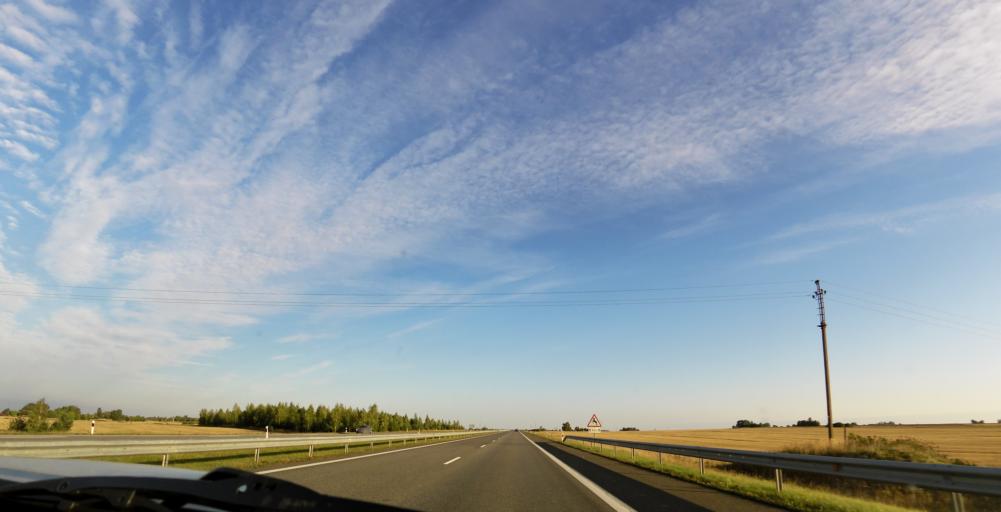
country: LT
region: Vilnius County
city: Ukmerge
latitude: 55.2824
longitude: 24.8049
